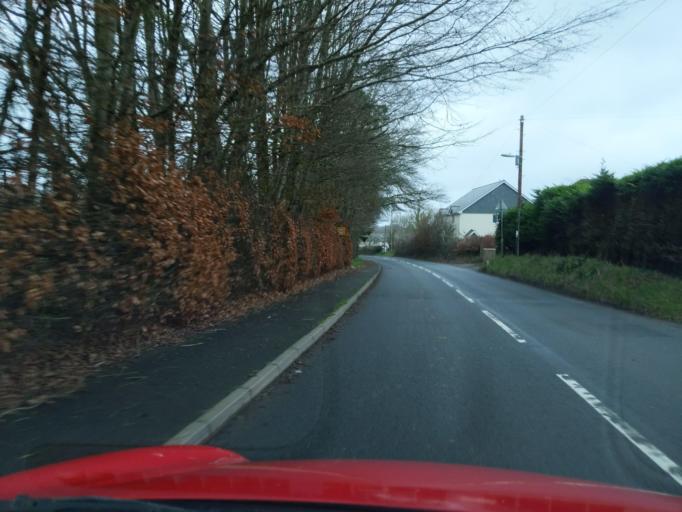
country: GB
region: England
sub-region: Devon
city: Holsworthy
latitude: 50.7682
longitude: -4.3364
